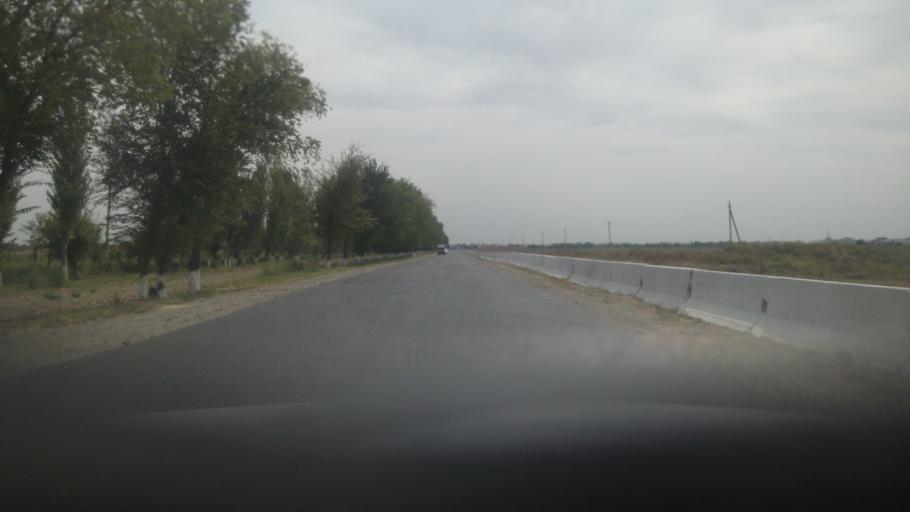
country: UZ
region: Sirdaryo
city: Guliston
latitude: 40.5150
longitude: 68.7940
